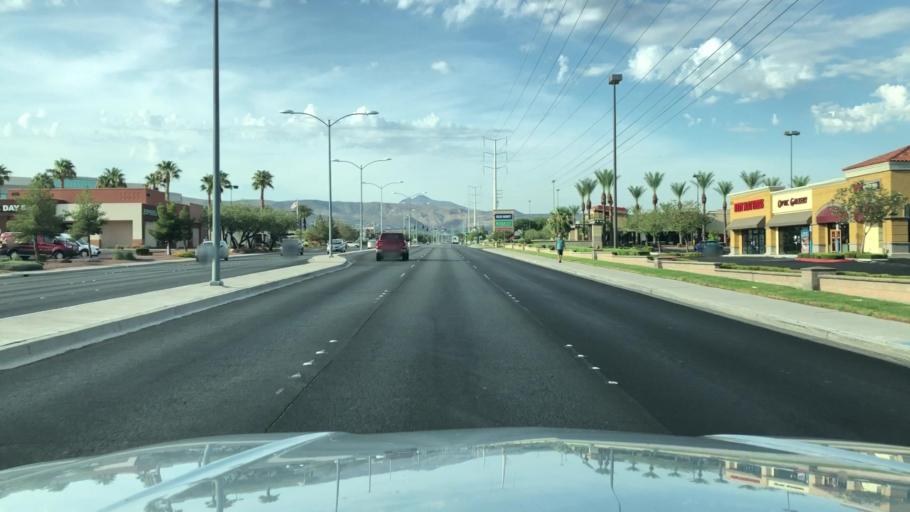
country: US
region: Nevada
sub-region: Clark County
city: Whitney
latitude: 36.0593
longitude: -115.0463
